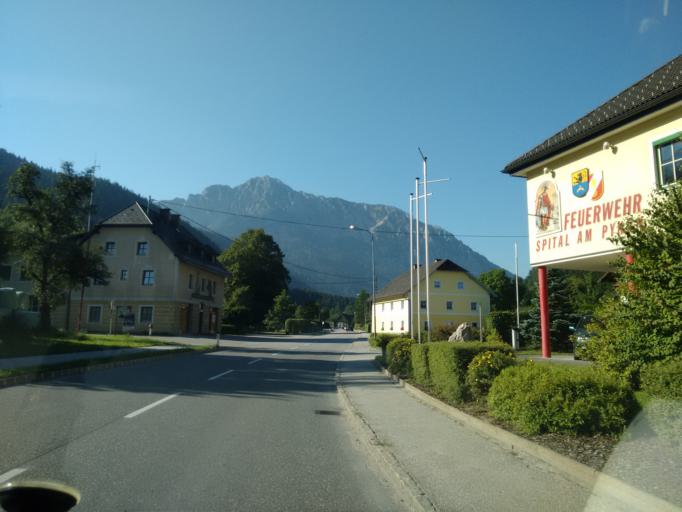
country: AT
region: Upper Austria
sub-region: Politischer Bezirk Kirchdorf an der Krems
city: Rossleithen
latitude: 47.6632
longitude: 14.3396
